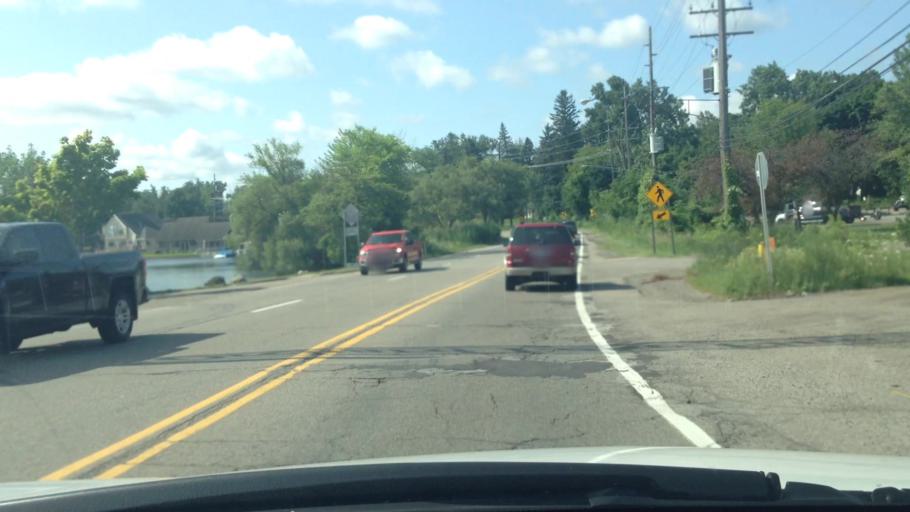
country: US
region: Michigan
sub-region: Oakland County
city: Wolverine Lake
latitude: 42.6122
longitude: -83.4469
